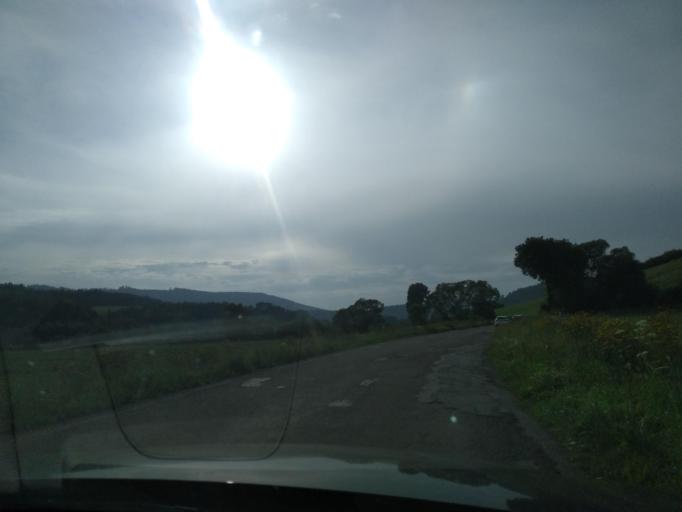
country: PL
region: Subcarpathian Voivodeship
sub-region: Powiat sanocki
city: Tyrawa Woloska
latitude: 49.6044
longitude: 22.3076
